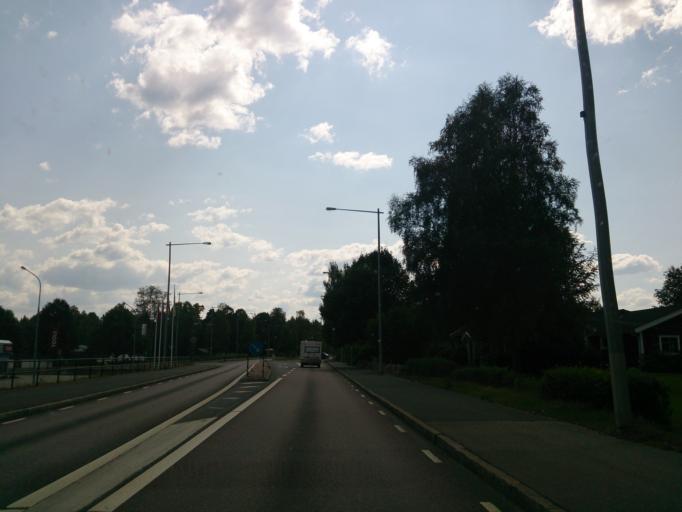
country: SE
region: Joenkoeping
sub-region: Gislaveds Kommun
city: Smalandsstenar
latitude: 57.1535
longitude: 13.4010
